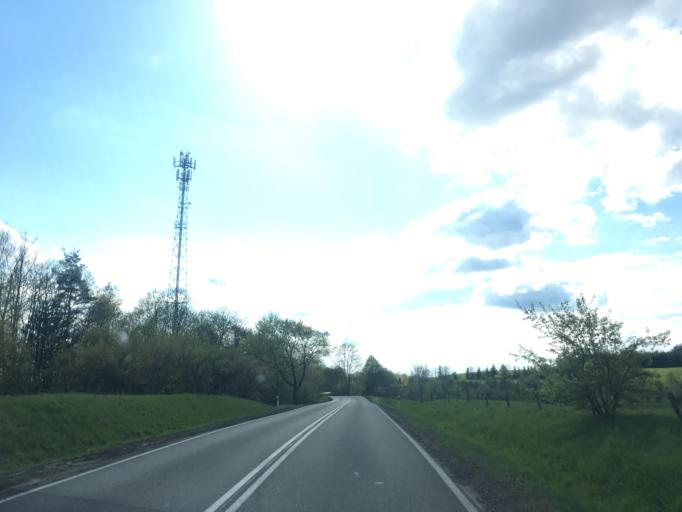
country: PL
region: Warmian-Masurian Voivodeship
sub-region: Powiat szczycienski
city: Jedwabno
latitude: 53.5342
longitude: 20.7495
